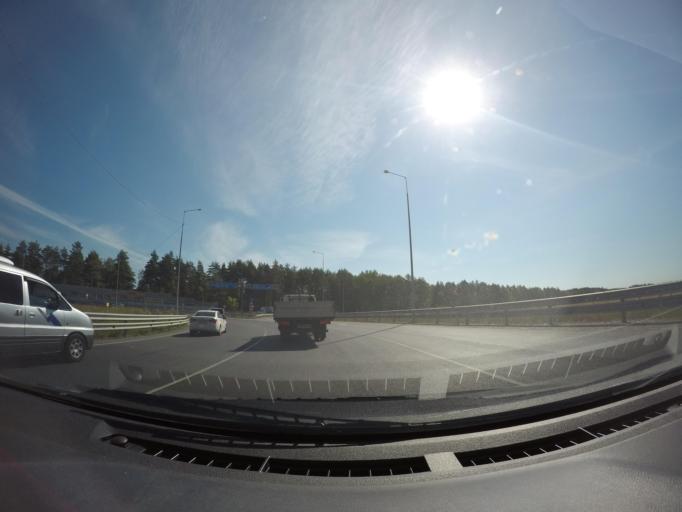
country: RU
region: Moskovskaya
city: Gzhel'
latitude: 55.6237
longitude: 38.3647
